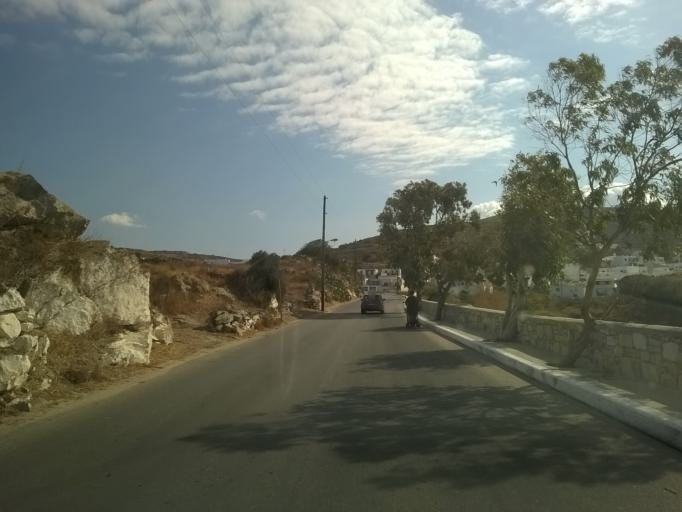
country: GR
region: South Aegean
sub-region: Nomos Kykladon
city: Naxos
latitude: 37.0599
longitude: 25.4061
